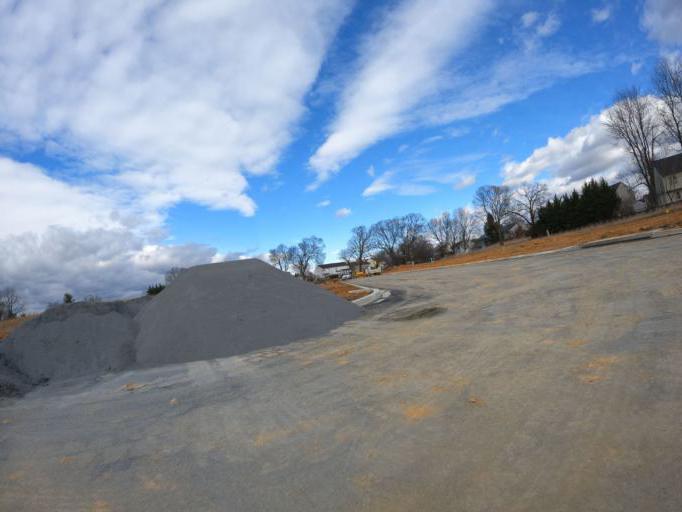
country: US
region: Maryland
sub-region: Frederick County
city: Ballenger Creek
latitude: 39.3792
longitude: -77.4326
